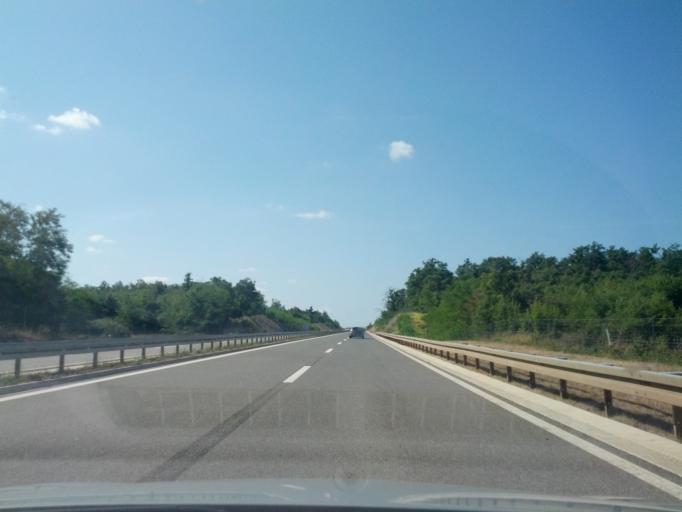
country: HR
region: Istarska
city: Vrsar
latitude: 45.1993
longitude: 13.7298
